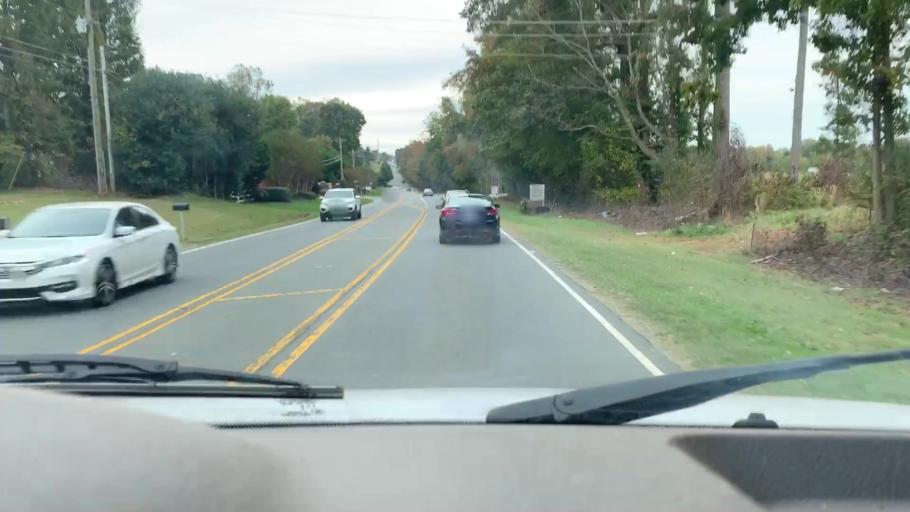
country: US
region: North Carolina
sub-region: Mecklenburg County
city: Huntersville
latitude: 35.4322
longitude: -80.8644
